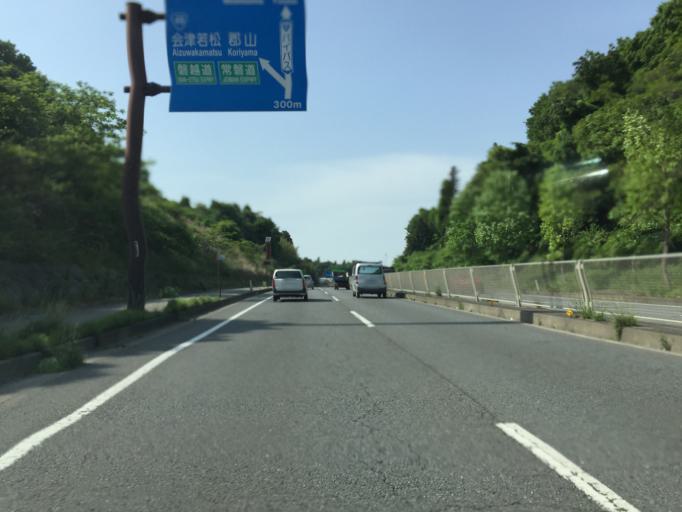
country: JP
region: Fukushima
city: Iwaki
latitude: 37.0160
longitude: 140.8945
